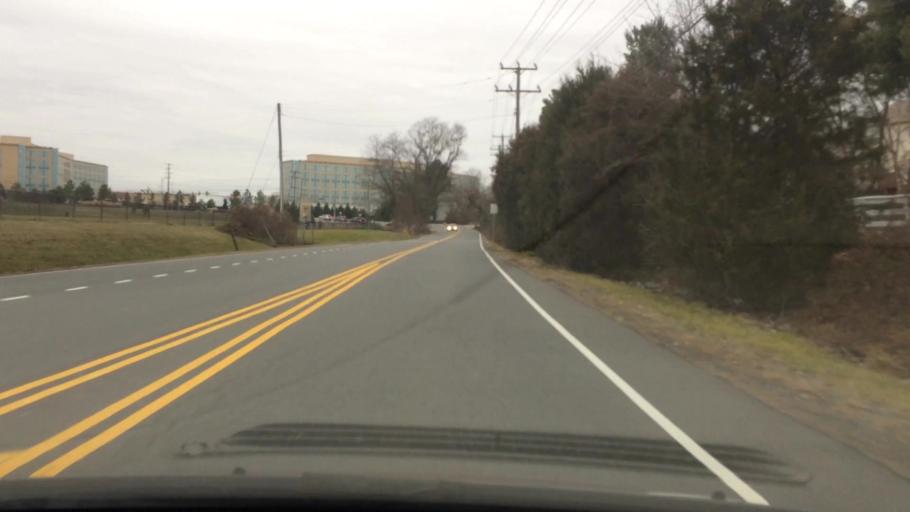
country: US
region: Virginia
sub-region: Fairfax County
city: Chantilly
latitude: 38.9090
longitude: -77.4198
